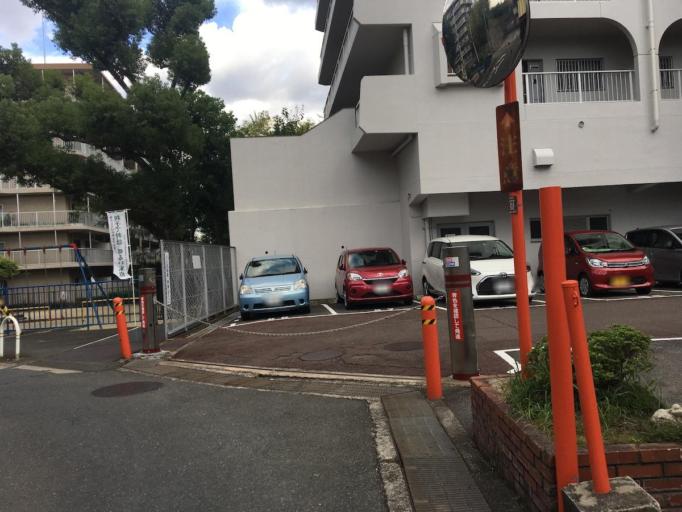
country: JP
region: Osaka
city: Suita
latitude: 34.7993
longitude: 135.5209
